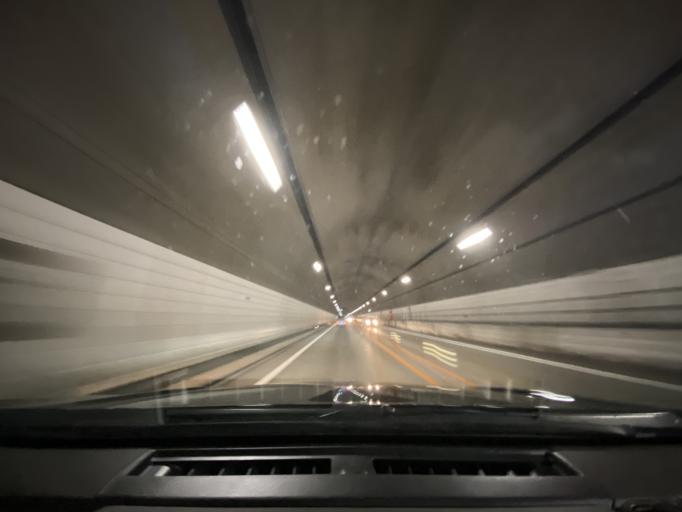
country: JP
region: Hokkaido
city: Shimo-furano
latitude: 43.0551
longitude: 142.5029
